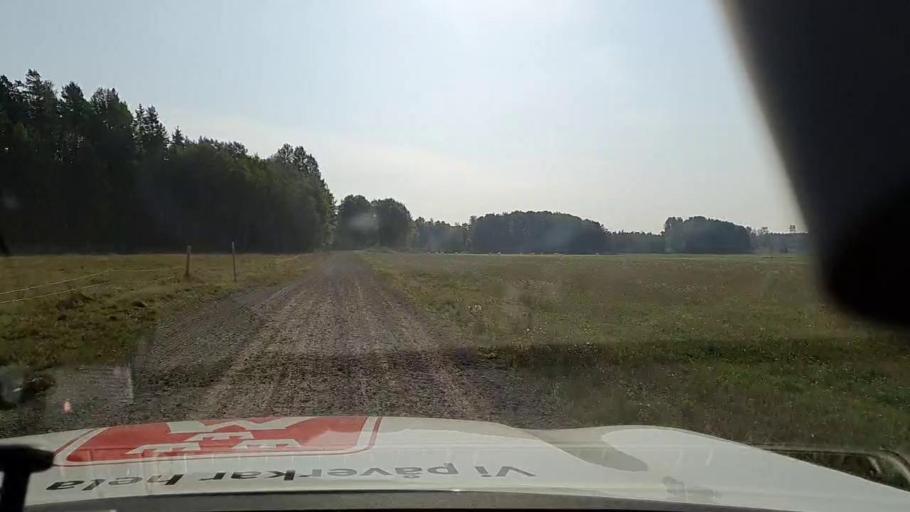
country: SE
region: Vaestmanland
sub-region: Kungsors Kommun
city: Kungsoer
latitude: 59.3514
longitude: 16.1632
